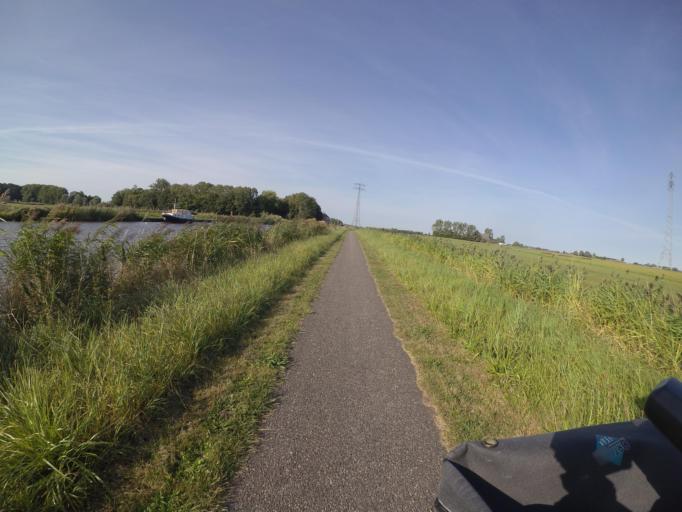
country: NL
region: Friesland
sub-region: Gemeente Dongeradeel
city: Dokkum
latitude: 53.3217
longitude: 5.9785
